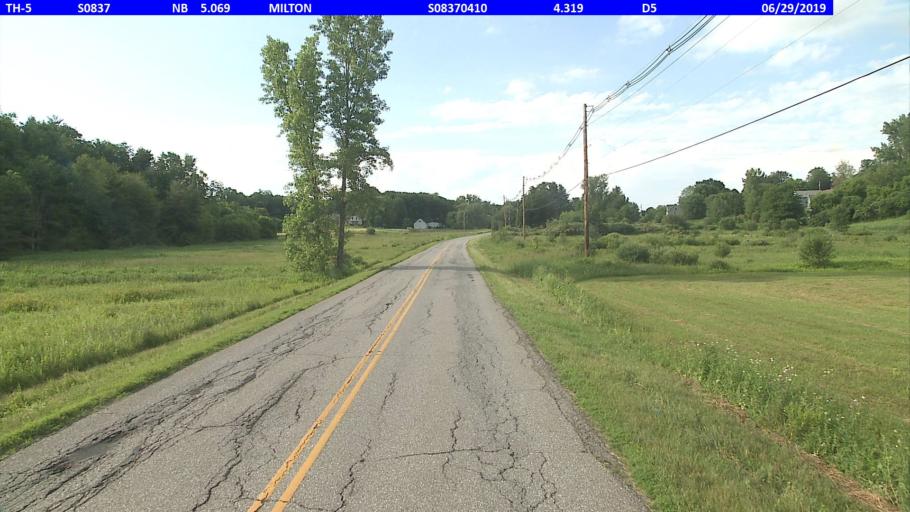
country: US
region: Vermont
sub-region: Chittenden County
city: Milton
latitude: 44.6348
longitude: -73.1014
